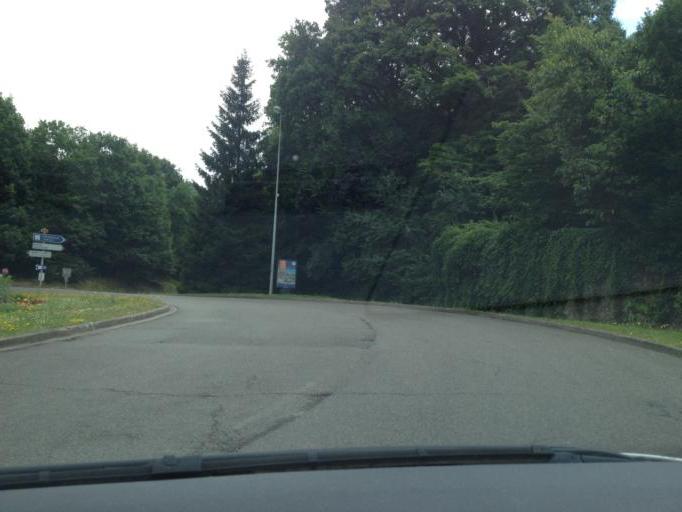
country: FR
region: Ile-de-France
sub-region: Departement de l'Essonne
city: Bures-sur-Yvette
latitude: 48.6952
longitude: 2.1695
